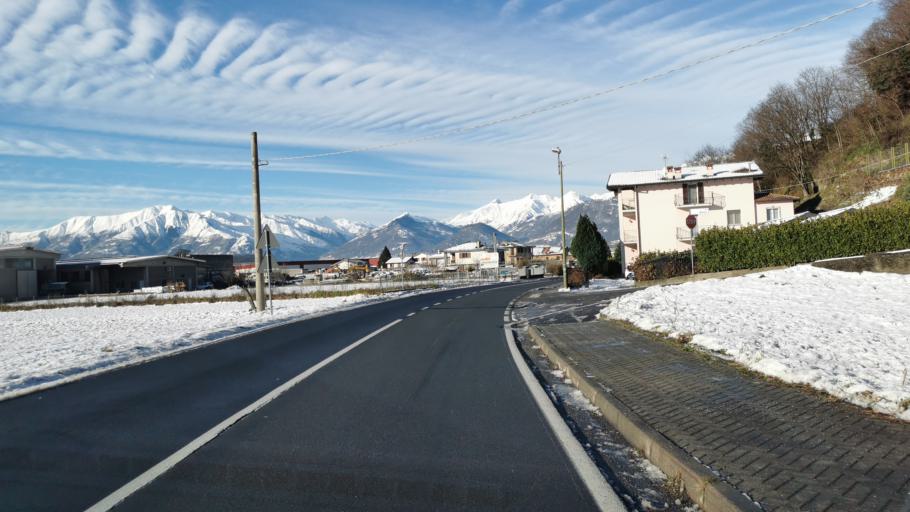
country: IT
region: Lombardy
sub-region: Provincia di Sondrio
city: Dubino
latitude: 46.1534
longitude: 9.4371
